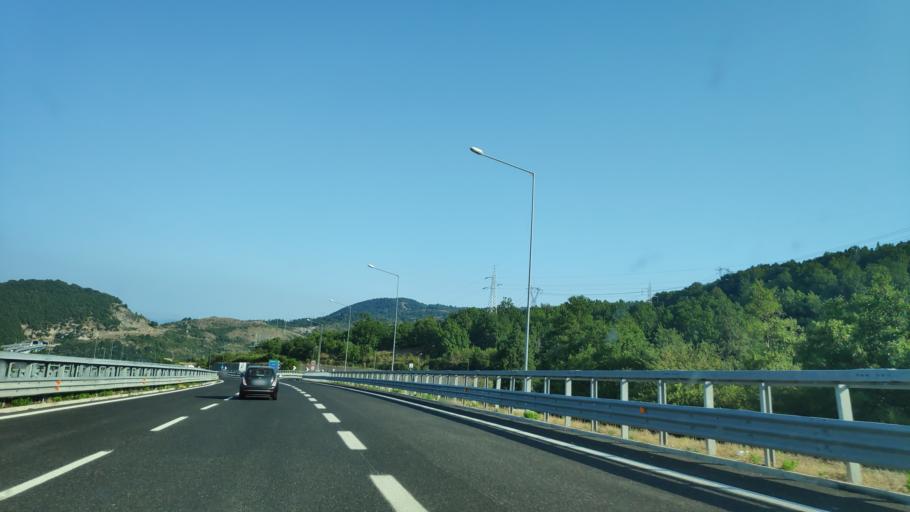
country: IT
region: Basilicate
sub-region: Provincia di Potenza
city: Lagonegro
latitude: 40.1514
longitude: 15.7497
